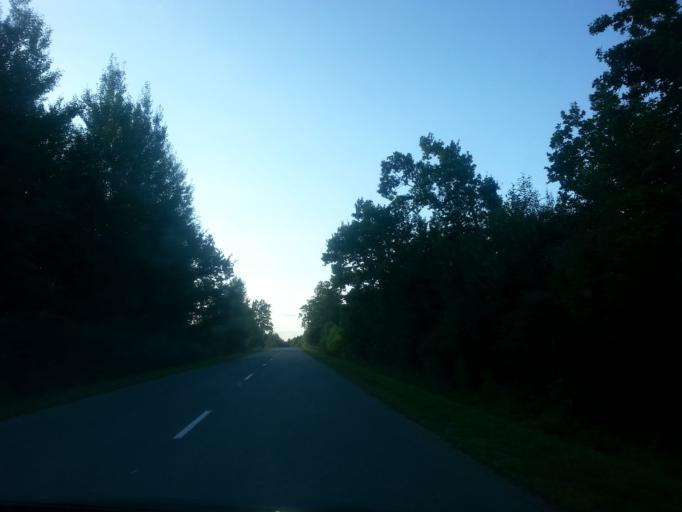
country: BY
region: Minsk
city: Narach
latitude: 55.0511
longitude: 26.6231
